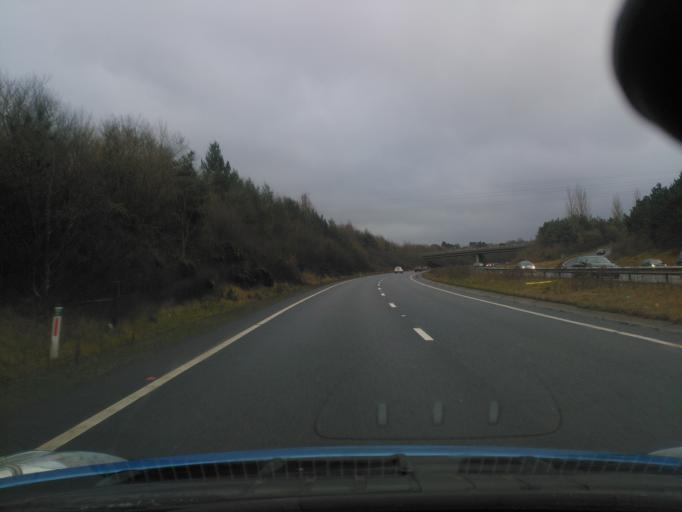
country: GB
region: England
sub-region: Surrey
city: Milford
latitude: 51.1813
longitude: -0.6510
